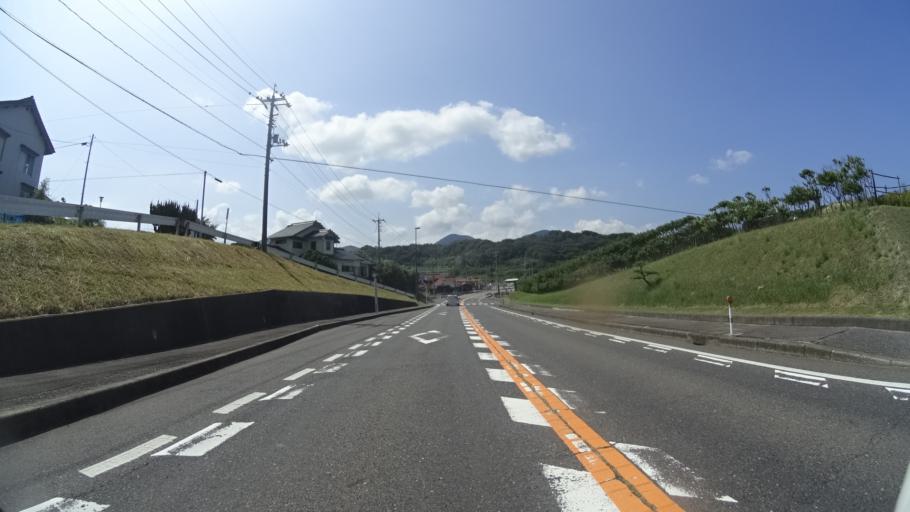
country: JP
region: Shimane
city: Masuda
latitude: 34.6724
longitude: 131.7524
